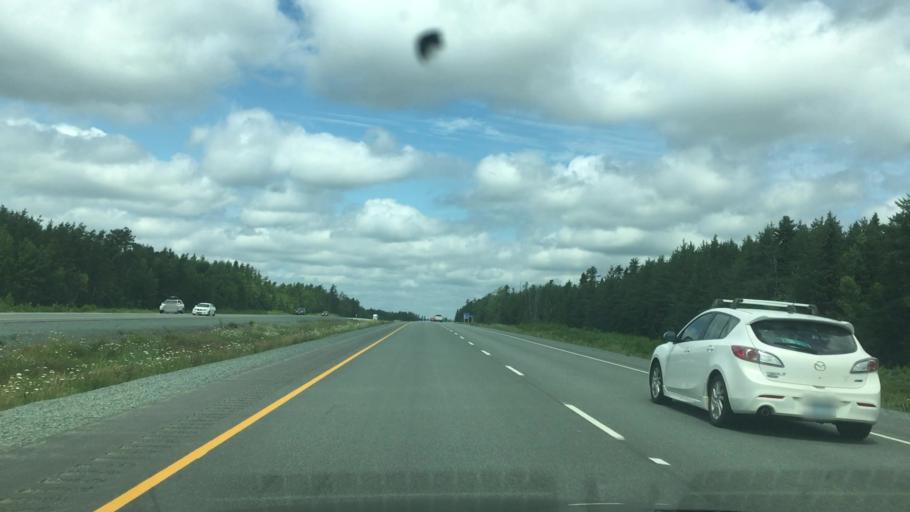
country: CA
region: Nova Scotia
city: Oxford
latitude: 45.6660
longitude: -63.7481
